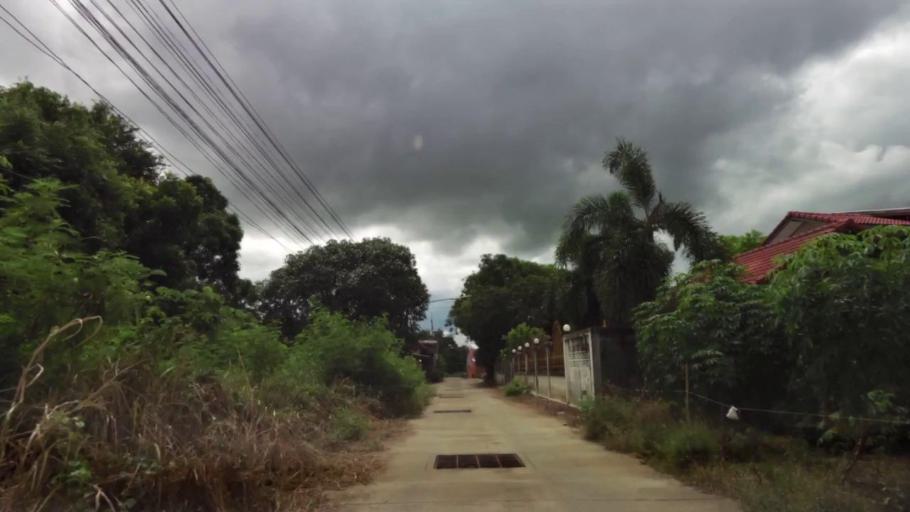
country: TH
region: Nakhon Sawan
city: Phai Sali
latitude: 15.6004
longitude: 100.6587
